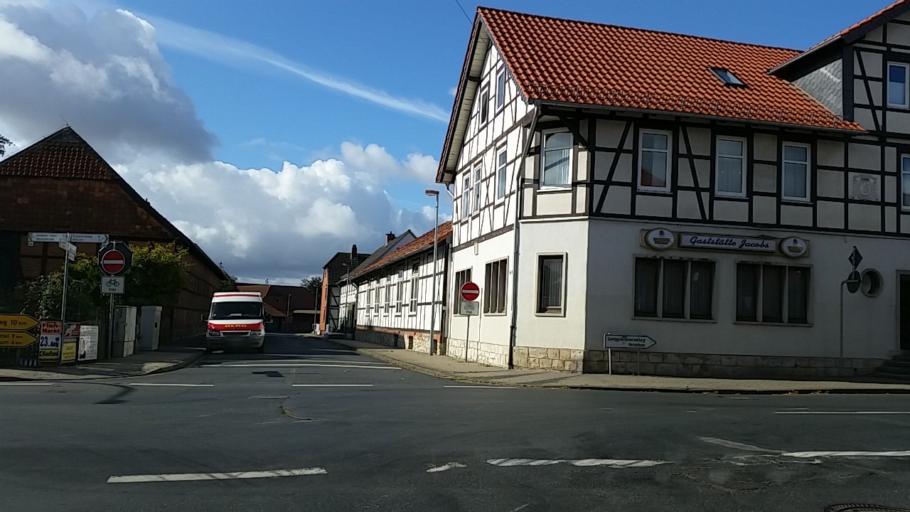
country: DE
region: Lower Saxony
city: Sickte
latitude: 52.2186
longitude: 10.6424
